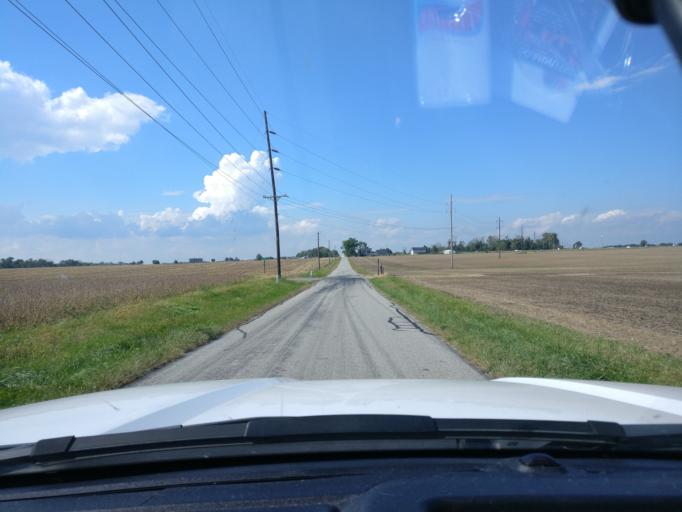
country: US
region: Ohio
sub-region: Warren County
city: Waynesville
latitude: 39.4635
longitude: -83.9701
